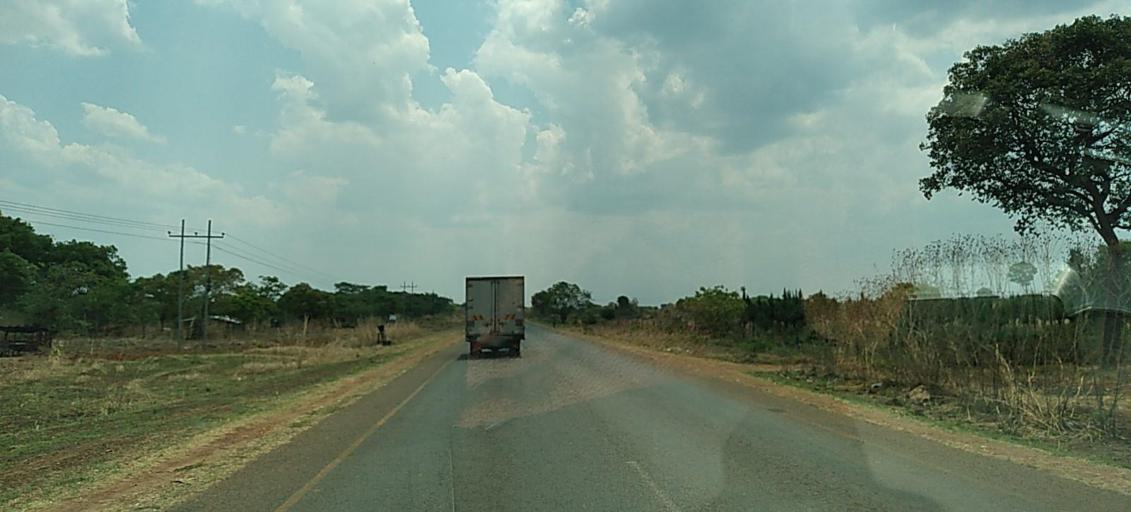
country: ZM
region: Copperbelt
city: Kalulushi
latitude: -12.8356
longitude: 27.9547
